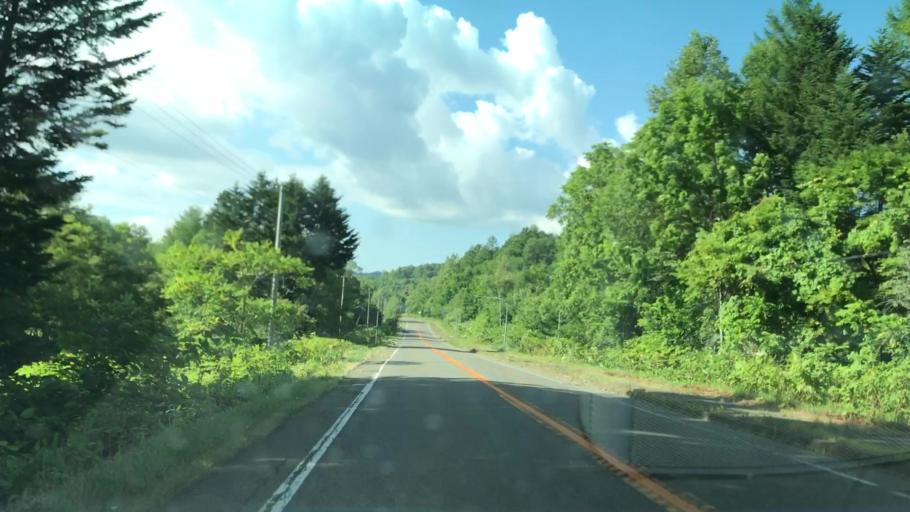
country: JP
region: Hokkaido
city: Shimo-furano
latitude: 42.8929
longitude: 142.4306
